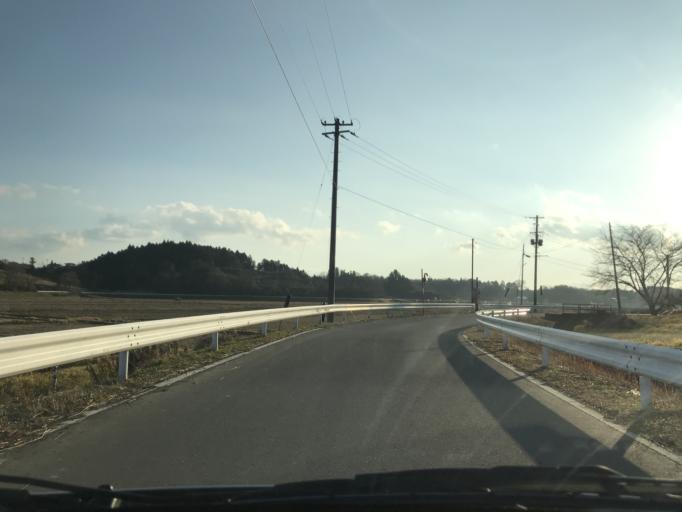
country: JP
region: Miyagi
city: Wakuya
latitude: 38.7078
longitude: 141.1277
